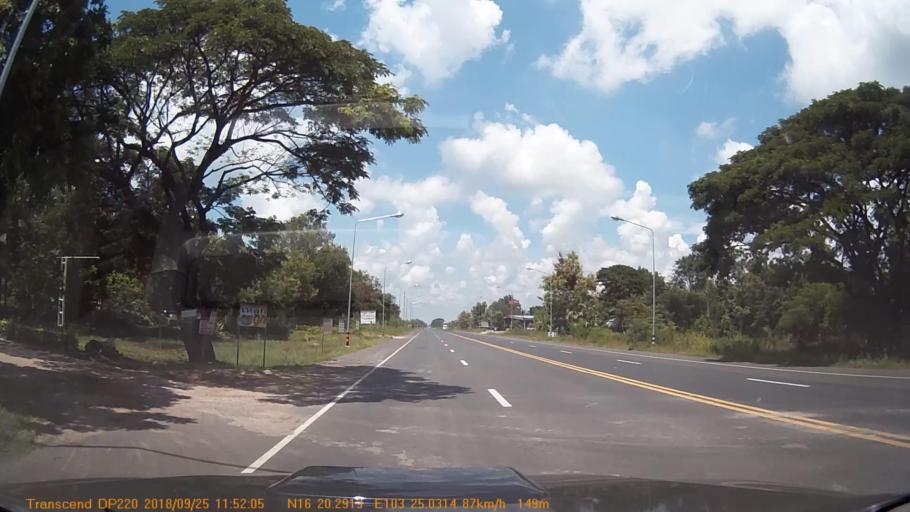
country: TH
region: Kalasin
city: Yang Talat
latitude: 16.3383
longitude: 103.4170
